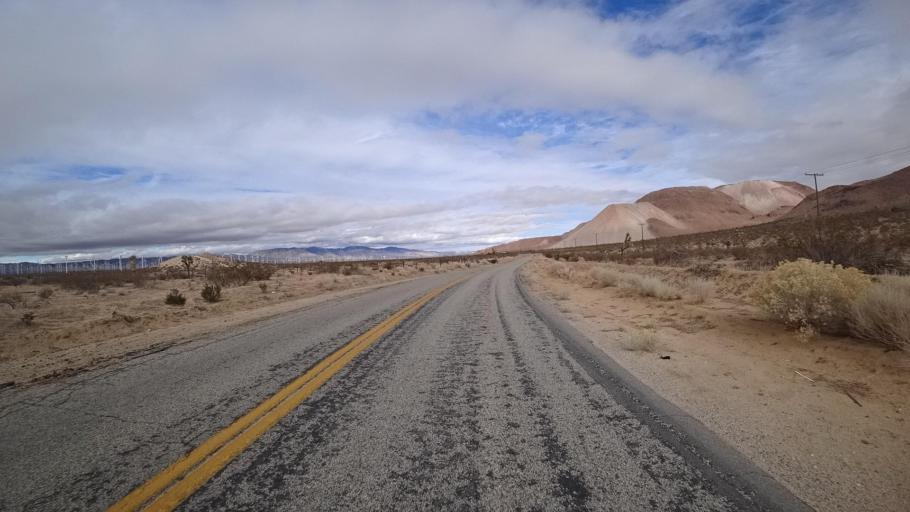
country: US
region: California
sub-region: Kern County
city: Mojave
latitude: 34.9663
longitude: -118.2127
